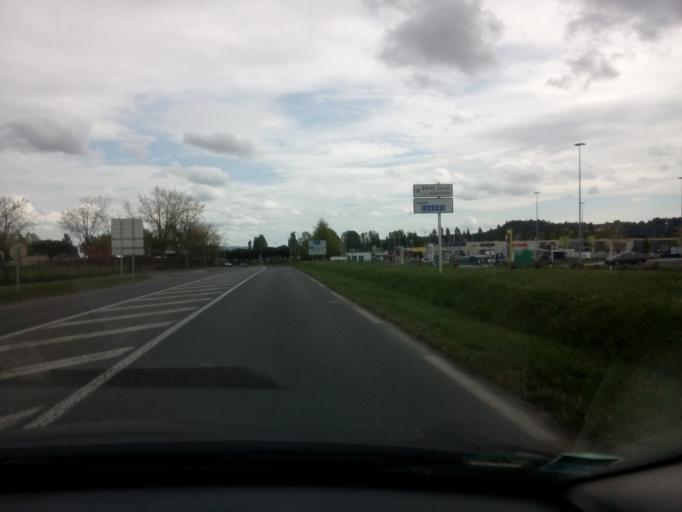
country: FR
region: Limousin
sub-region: Departement de la Correze
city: Saint-Pantaleon-de-Larche
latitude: 45.1456
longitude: 1.4799
